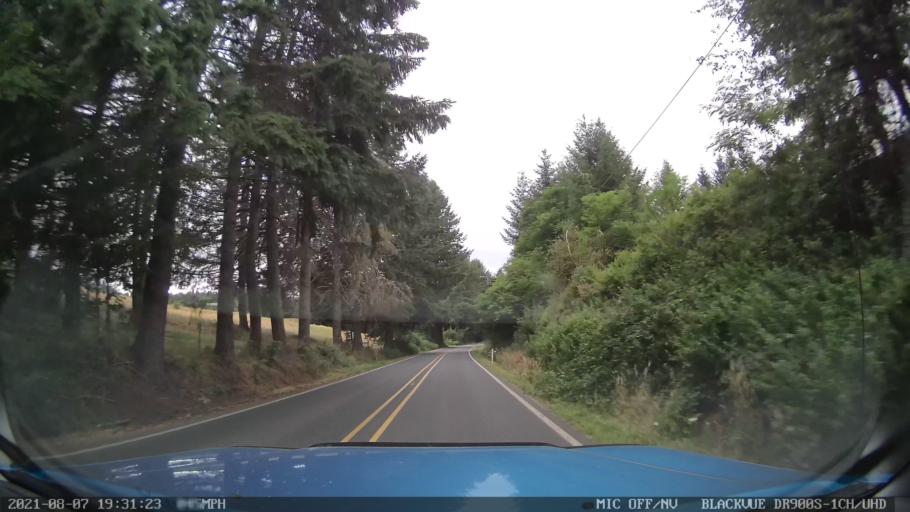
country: US
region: Oregon
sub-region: Linn County
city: Lyons
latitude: 44.8912
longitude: -122.6329
